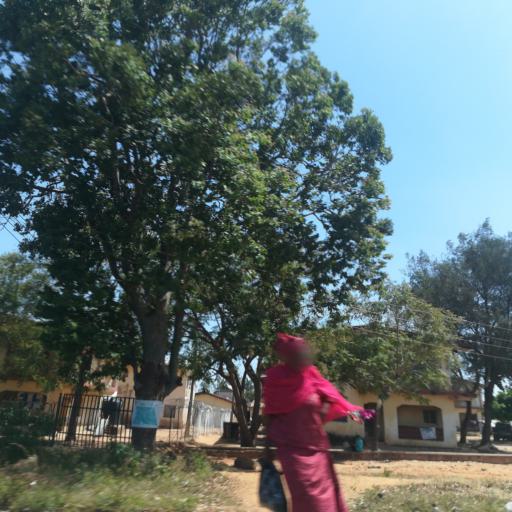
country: NG
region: Plateau
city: Bukuru
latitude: 9.8062
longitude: 8.8677
